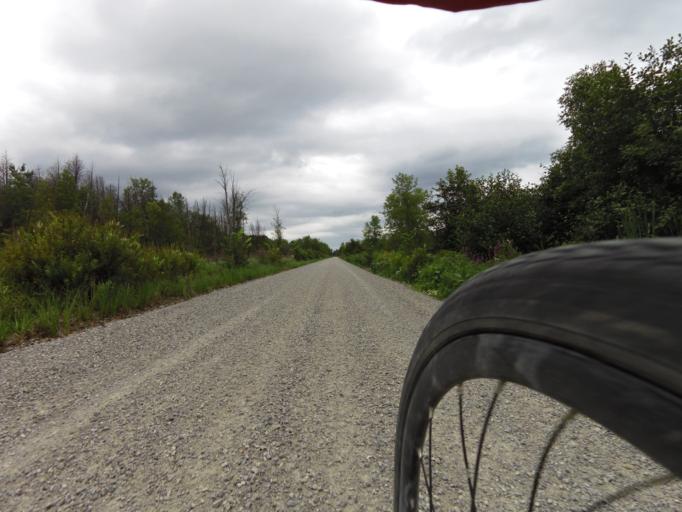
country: CA
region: Ontario
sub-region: Lanark County
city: Smiths Falls
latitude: 44.9443
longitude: -76.0411
